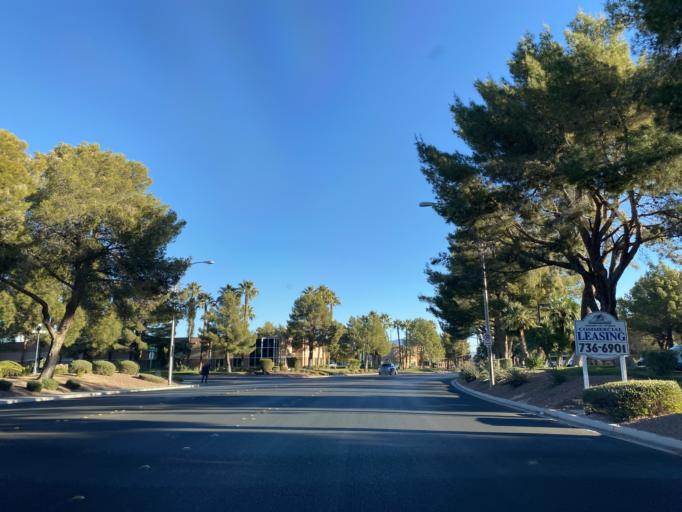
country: US
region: Nevada
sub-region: Clark County
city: Whitney
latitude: 36.0738
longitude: -115.1122
